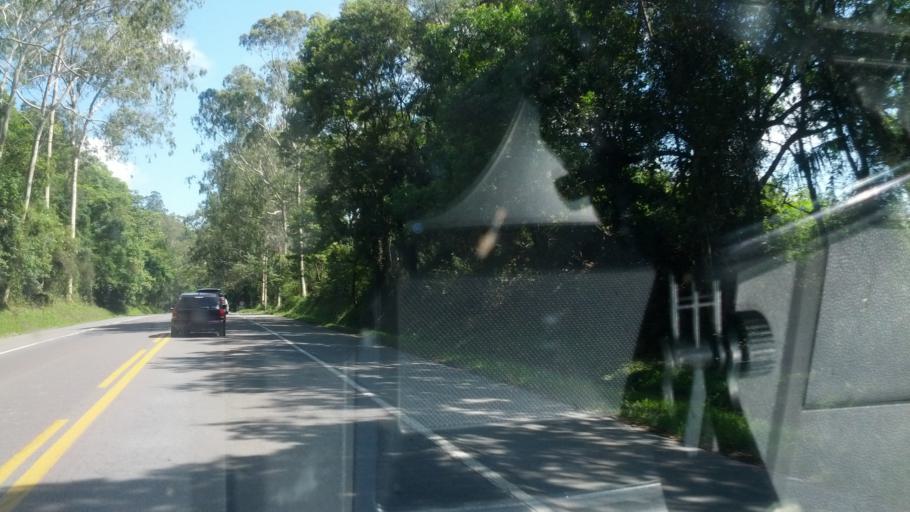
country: BR
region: Santa Catarina
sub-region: Ibirama
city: Ibirama
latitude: -27.1539
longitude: -49.5565
